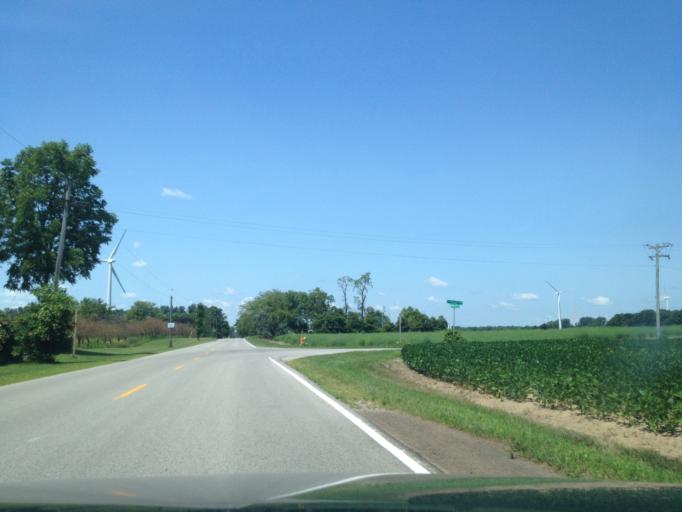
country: CA
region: Ontario
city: Aylmer
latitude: 42.6117
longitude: -80.6906
